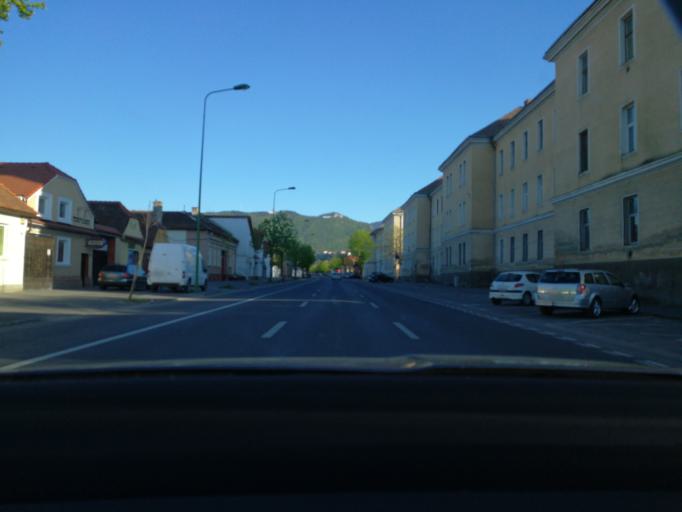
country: RO
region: Brasov
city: Brasov
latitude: 45.6613
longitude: 25.5790
